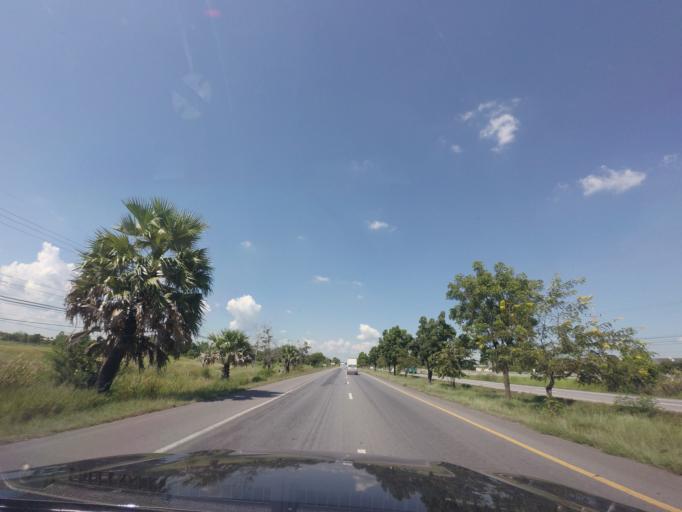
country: TH
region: Nakhon Ratchasima
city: Non Sung
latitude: 15.1625
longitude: 102.3314
